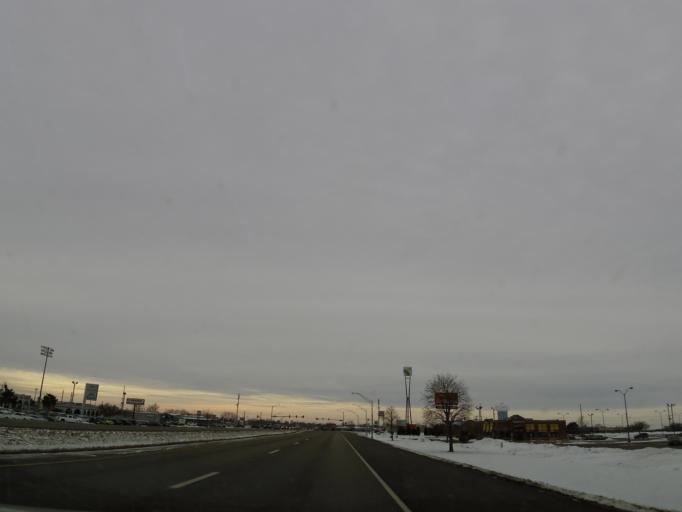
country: US
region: Illinois
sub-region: LaSalle County
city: Peru
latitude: 41.3556
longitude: -89.1256
